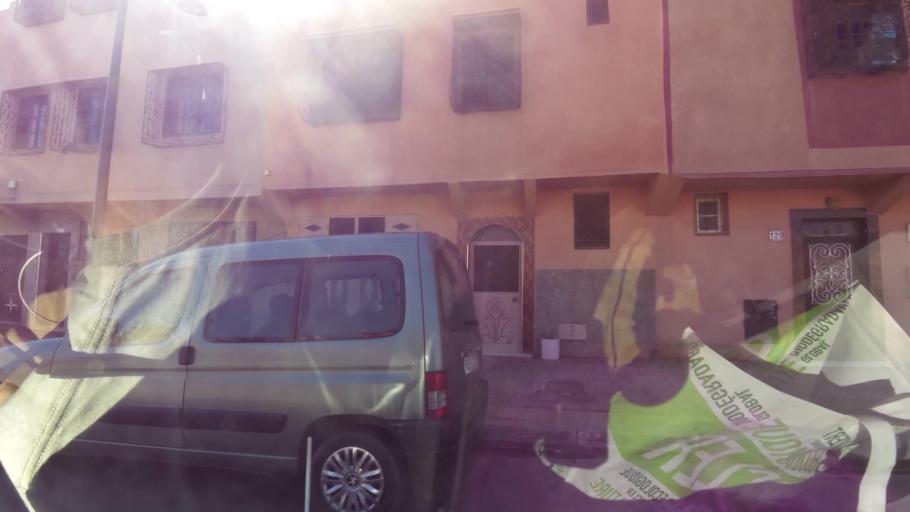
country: MA
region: Marrakech-Tensift-Al Haouz
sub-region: Marrakech
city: Marrakesh
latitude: 31.5911
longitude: -8.0503
